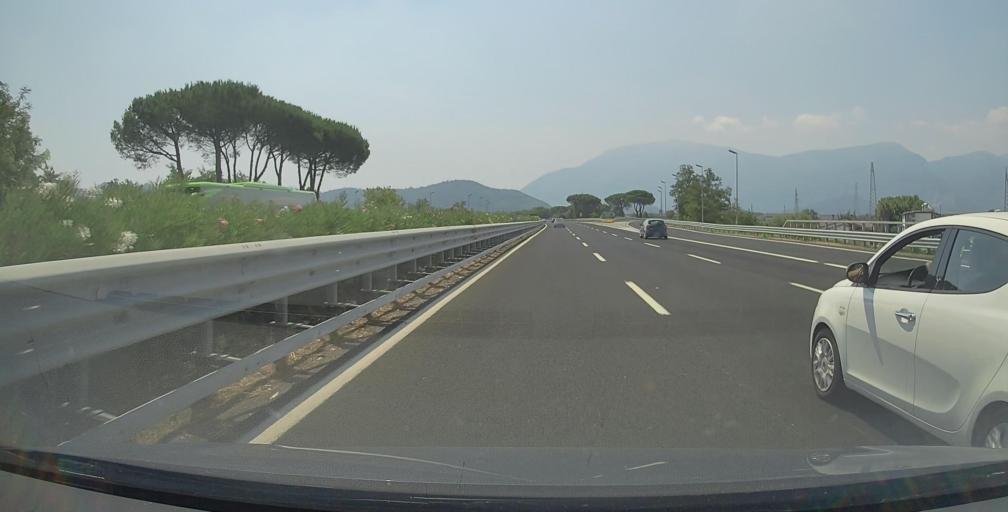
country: IT
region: Campania
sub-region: Provincia di Salerno
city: San Valentino Torio
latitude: 40.7876
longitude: 14.6180
